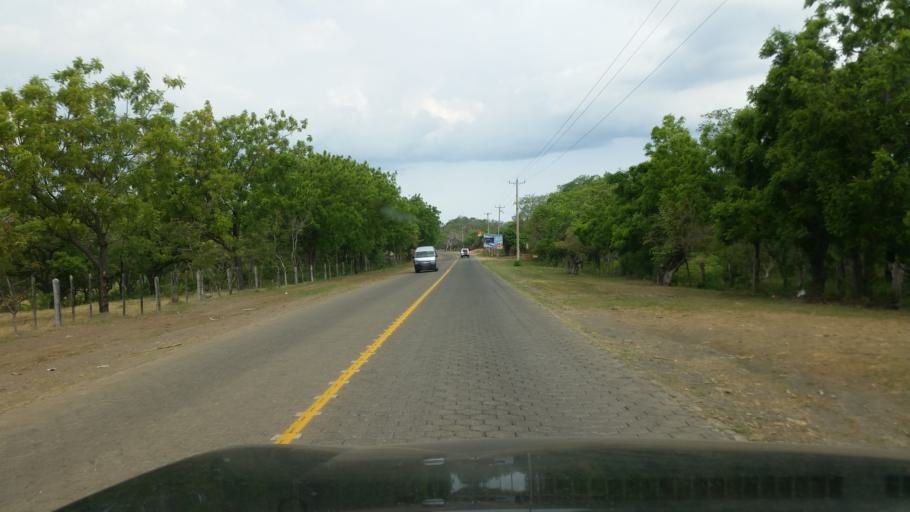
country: NI
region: Managua
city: Masachapa
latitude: 11.8360
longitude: -86.5113
